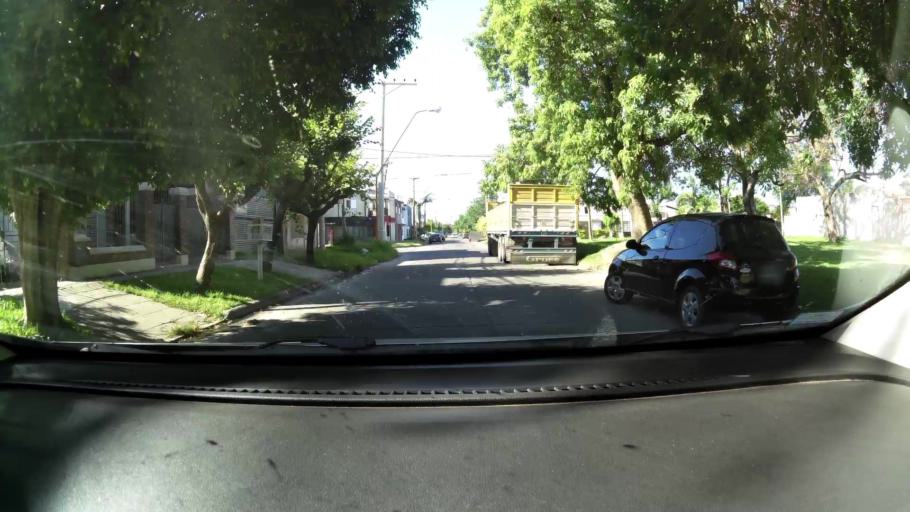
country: AR
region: Santa Fe
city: Santa Fe de la Vera Cruz
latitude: -31.6058
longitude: -60.6829
